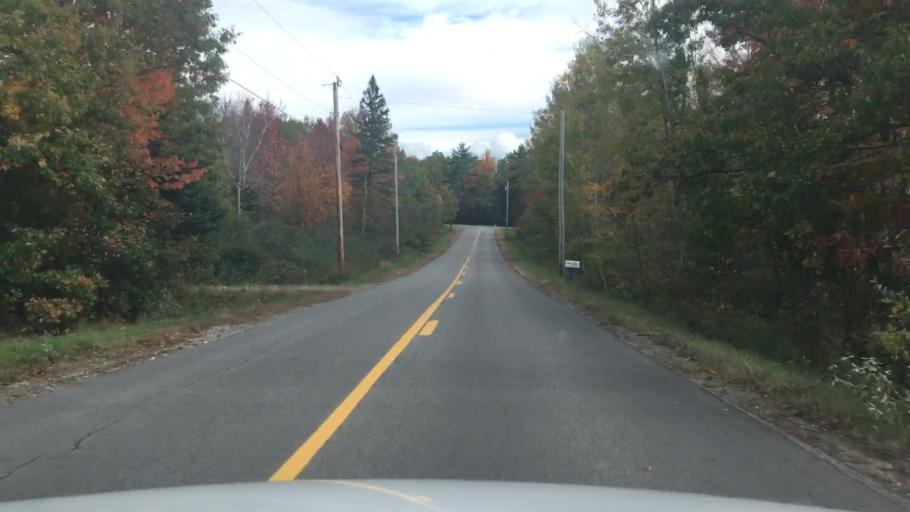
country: US
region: Maine
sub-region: Waldo County
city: Searsmont
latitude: 44.3797
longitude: -69.1337
